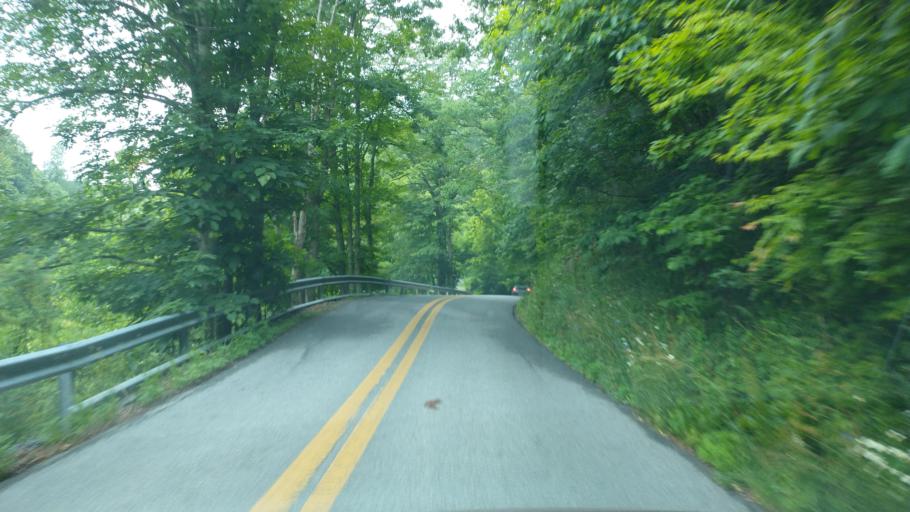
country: US
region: West Virginia
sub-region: Mercer County
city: Athens
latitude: 37.4280
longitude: -80.9916
